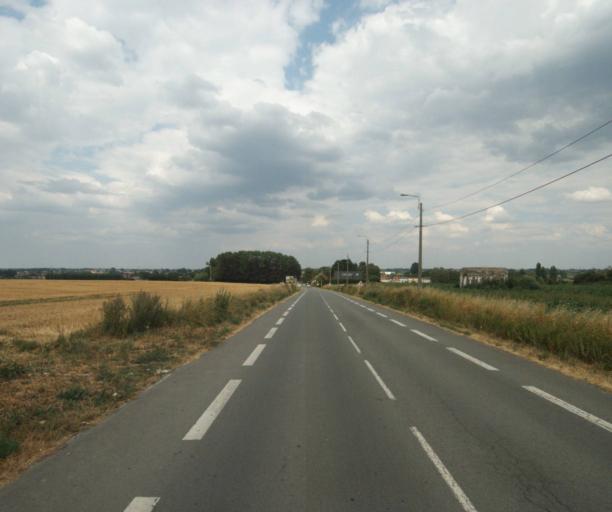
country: FR
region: Nord-Pas-de-Calais
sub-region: Departement du Nord
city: Neuville-en-Ferrain
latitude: 50.7668
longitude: 3.1594
